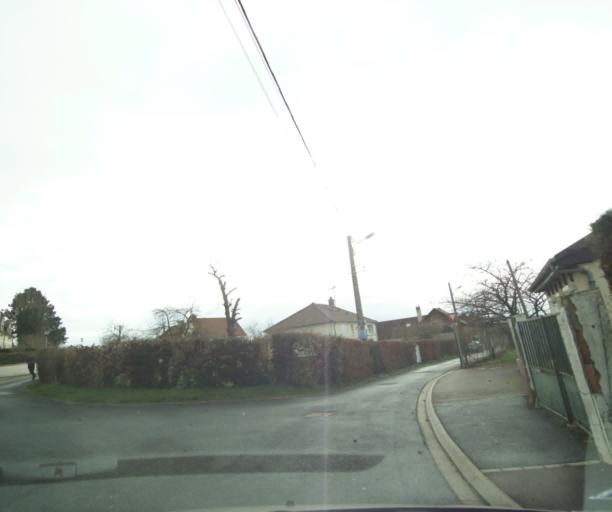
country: FR
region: Picardie
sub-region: Departement de l'Oise
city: Noyon
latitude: 49.5861
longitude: 2.9953
